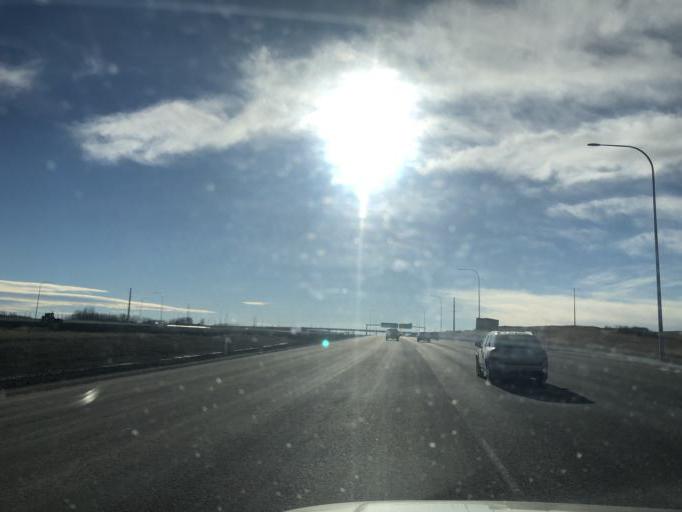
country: CA
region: Alberta
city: Calgary
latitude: 50.9838
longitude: -114.1646
